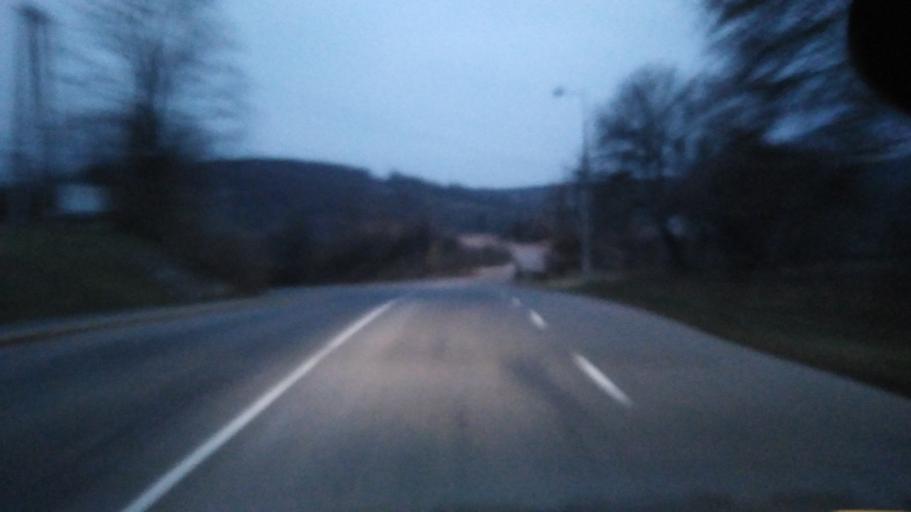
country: HU
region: Nograd
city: Salgotarjan
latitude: 48.1085
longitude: 19.7902
